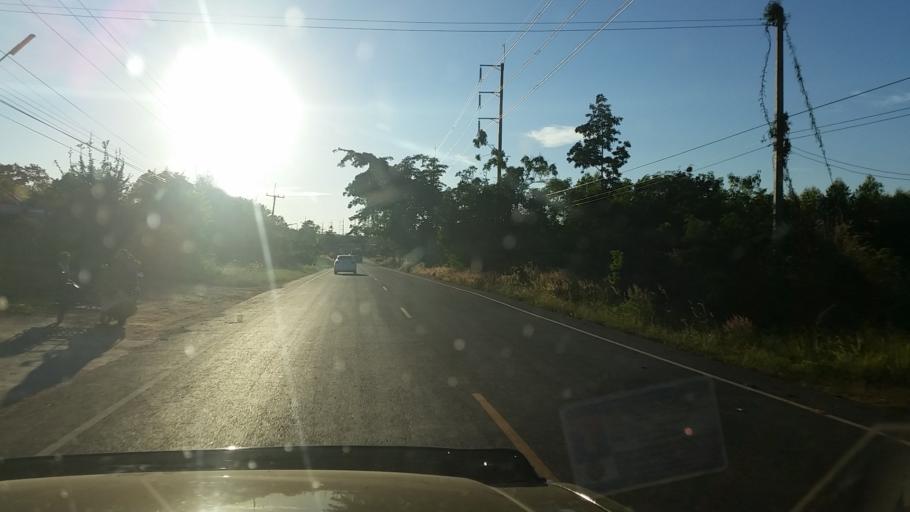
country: TH
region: Chaiyaphum
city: Sap Yai
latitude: 15.6827
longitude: 101.6982
